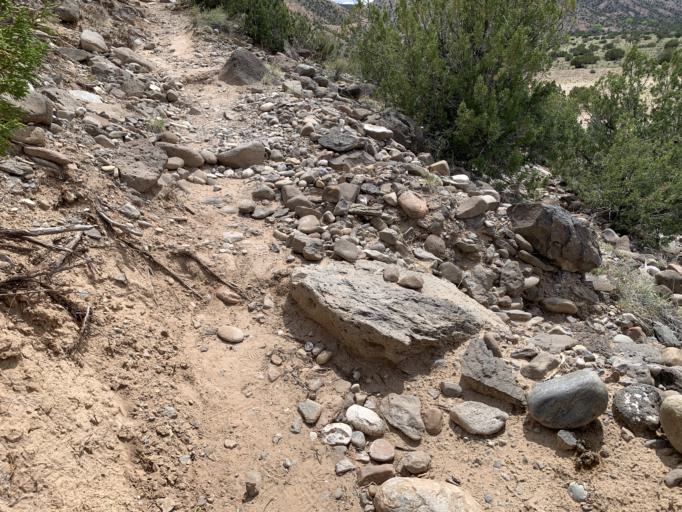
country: US
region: New Mexico
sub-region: Rio Arriba County
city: Ohkay Owingeh
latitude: 36.2125
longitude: -106.2771
